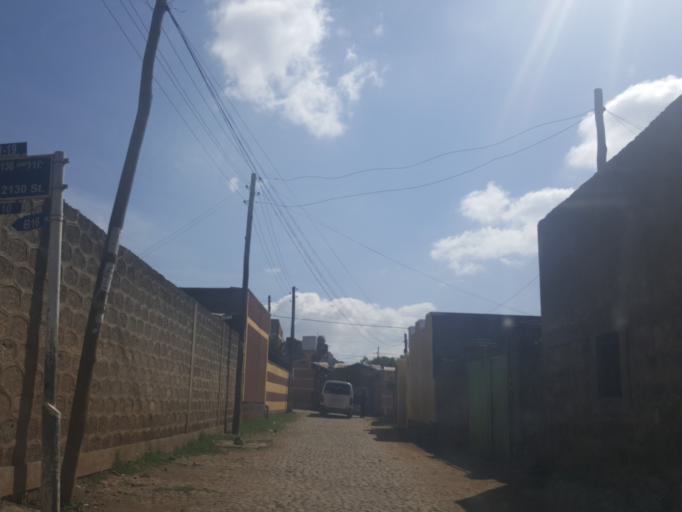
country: ET
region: Adis Abeba
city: Addis Ababa
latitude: 9.0660
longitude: 38.7246
